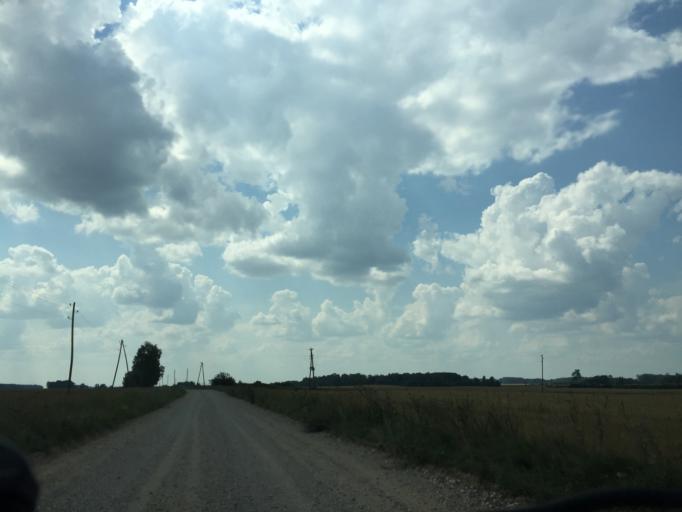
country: LT
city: Zagare
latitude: 56.3471
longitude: 23.1434
